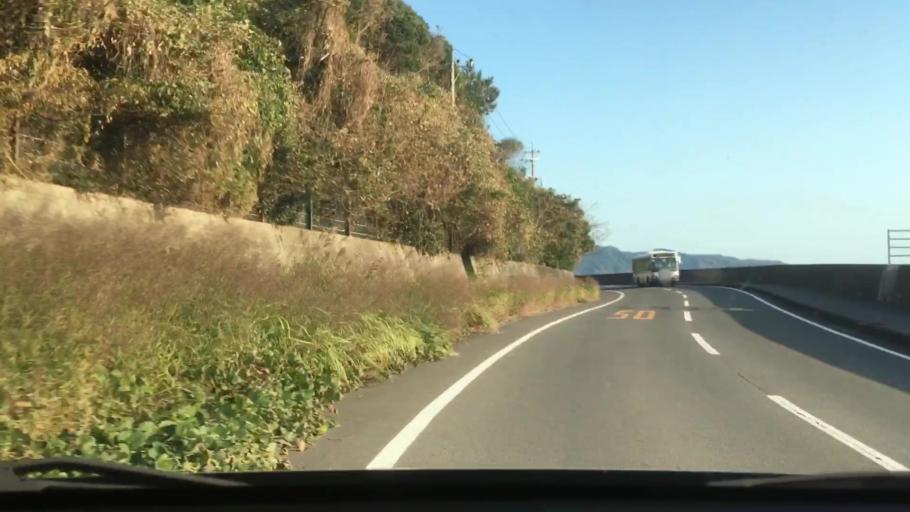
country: JP
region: Nagasaki
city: Sasebo
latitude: 33.0273
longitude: 129.5943
